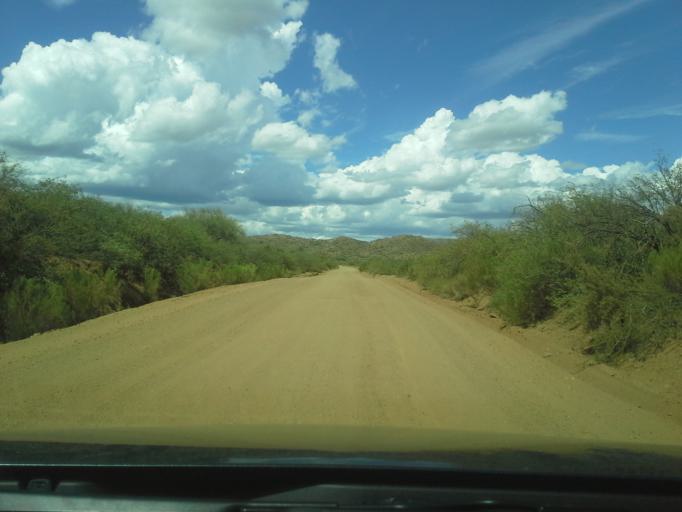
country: US
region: Arizona
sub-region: Yavapai County
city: Spring Valley
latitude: 34.2612
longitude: -112.1805
